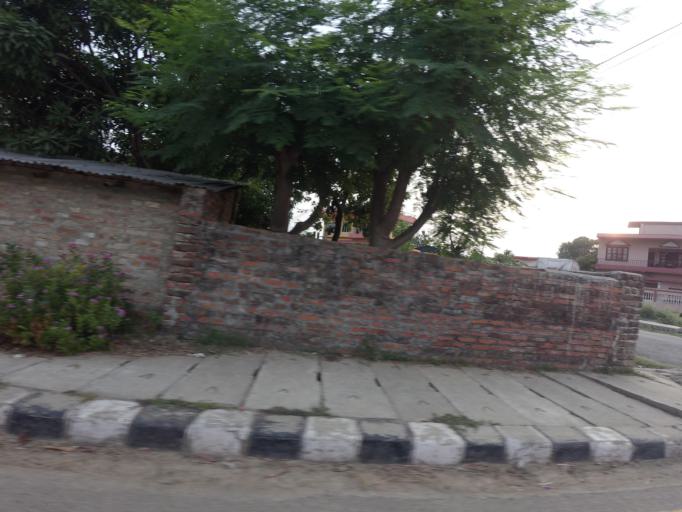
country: NP
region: Western Region
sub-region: Lumbini Zone
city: Bhairahawa
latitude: 27.5084
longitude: 83.4642
